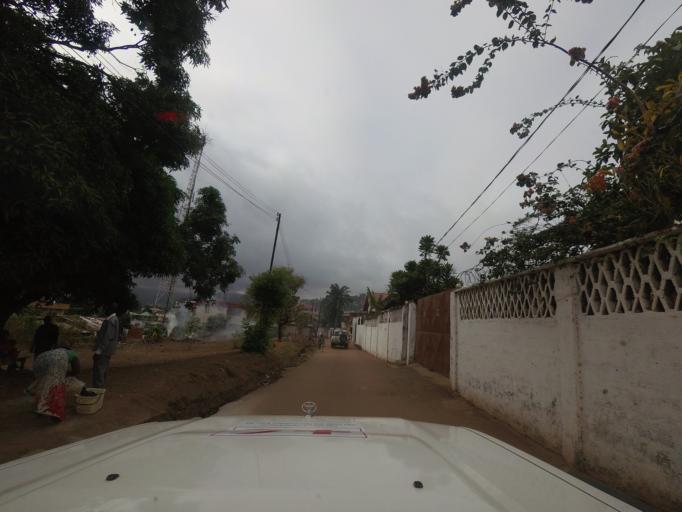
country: SL
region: Western Area
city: Freetown
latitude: 8.4874
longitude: -13.2646
